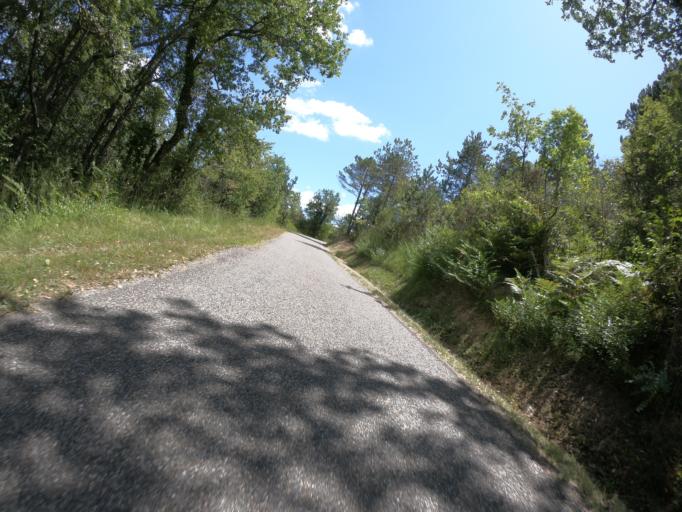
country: FR
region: Midi-Pyrenees
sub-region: Departement de l'Ariege
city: Mirepoix
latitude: 43.0603
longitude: 1.8426
